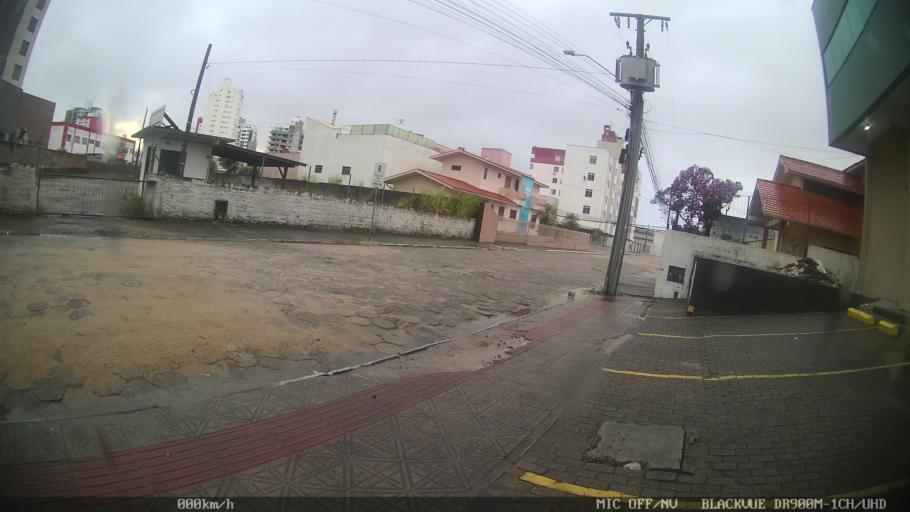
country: BR
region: Santa Catarina
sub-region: Sao Jose
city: Campinas
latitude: -27.5979
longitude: -48.6188
